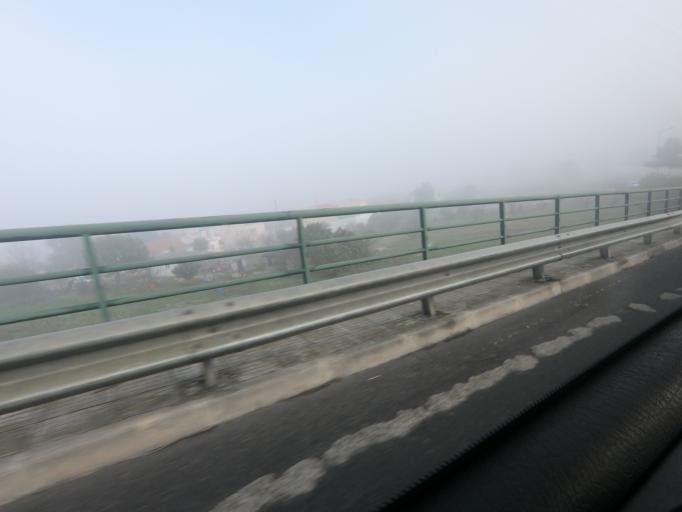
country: PT
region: Setubal
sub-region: Palmela
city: Pinhal Novo
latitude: 38.6072
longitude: -8.8880
